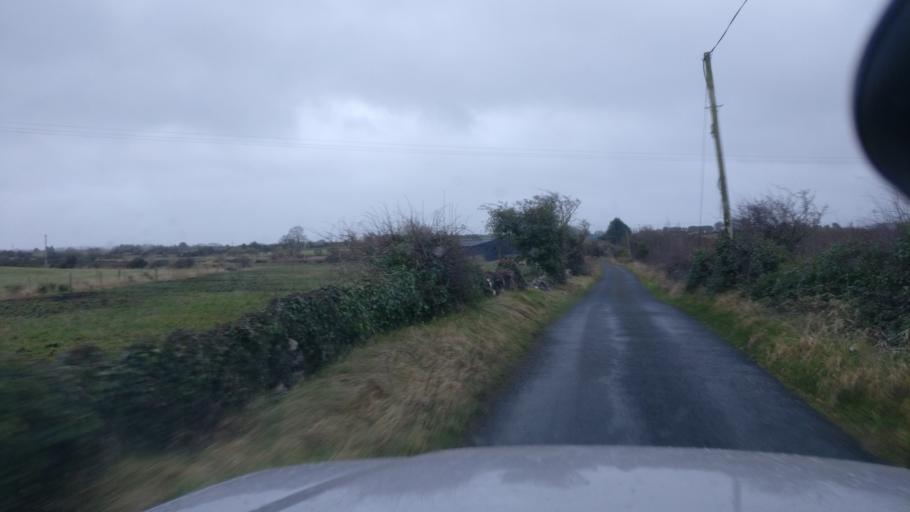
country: IE
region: Connaught
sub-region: County Galway
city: Loughrea
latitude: 53.2128
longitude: -8.5895
